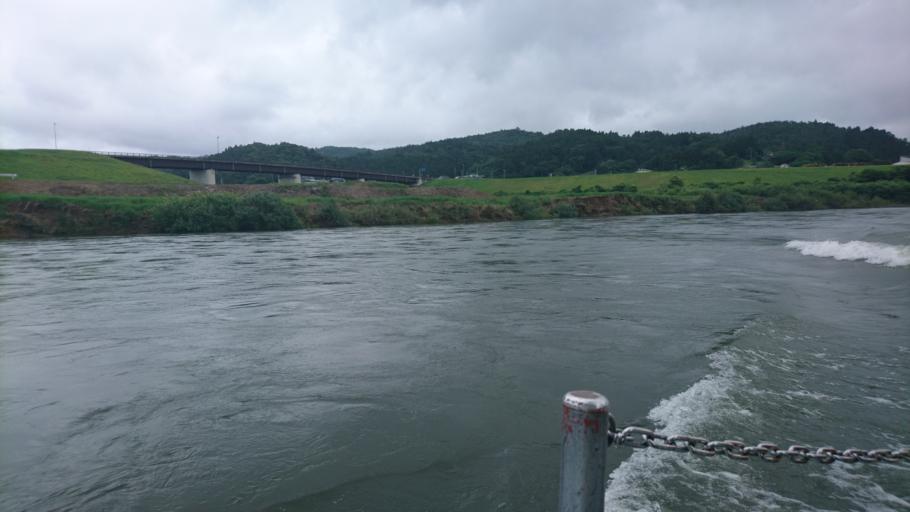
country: JP
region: Iwate
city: Ichinoseki
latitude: 38.9018
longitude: 141.2578
